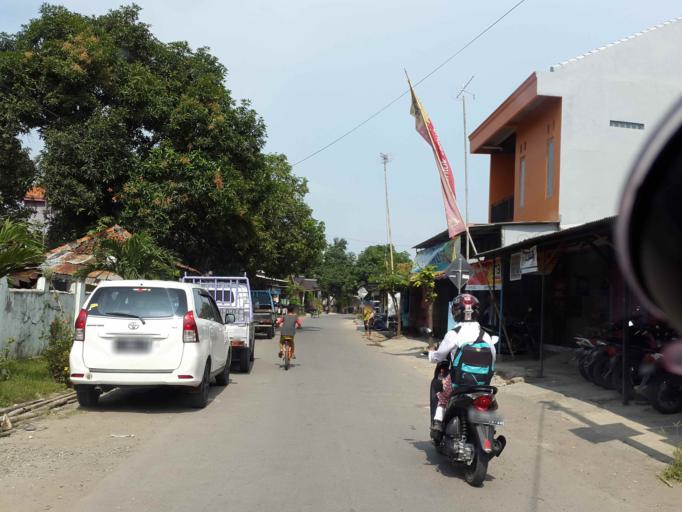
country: ID
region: Central Java
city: Pemalang
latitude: -6.9002
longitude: 109.3880
